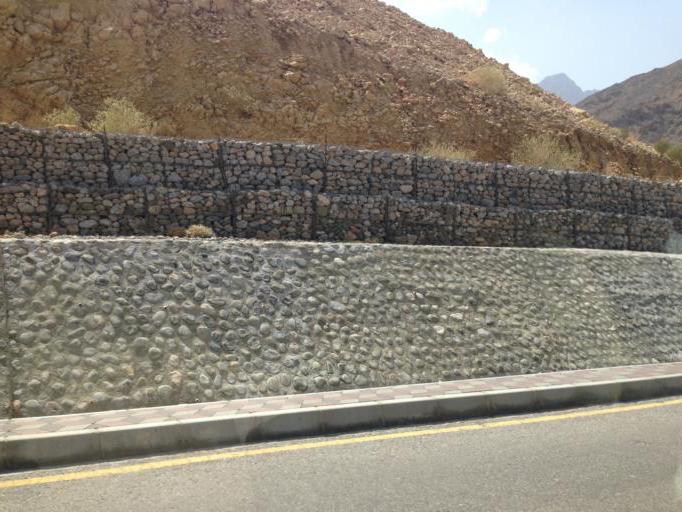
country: OM
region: Ash Sharqiyah
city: Ibra'
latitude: 23.0899
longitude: 58.8507
